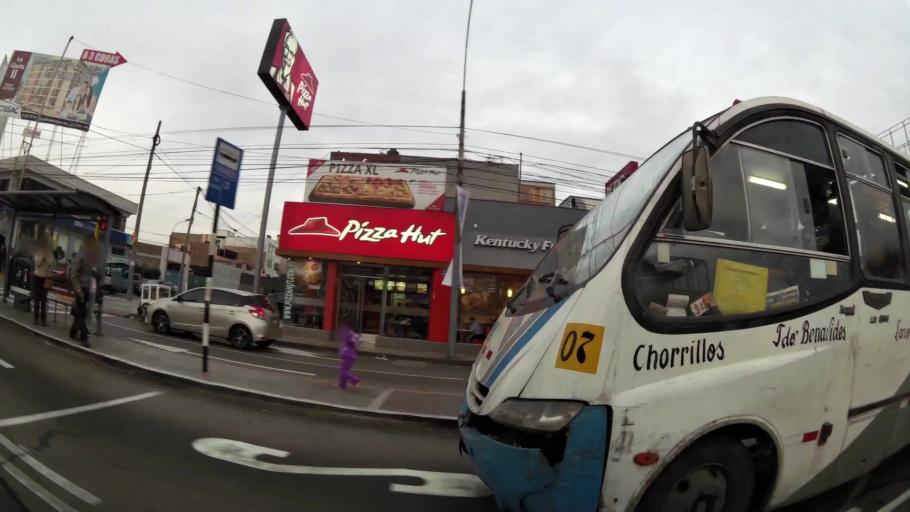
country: PE
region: Callao
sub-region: Callao
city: Callao
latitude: -12.0718
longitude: -77.0987
